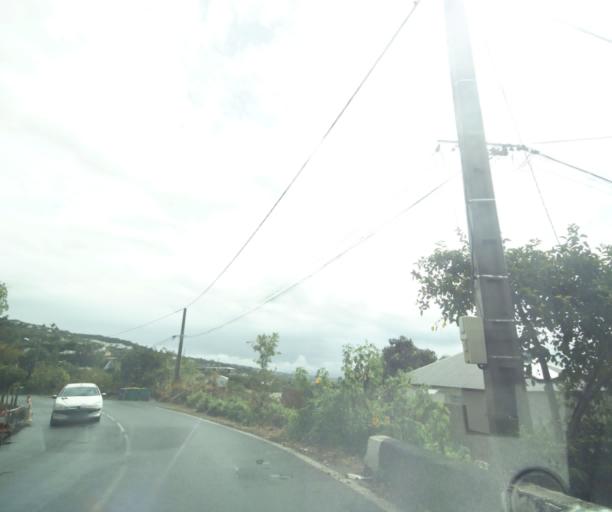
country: RE
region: Reunion
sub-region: Reunion
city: Saint-Paul
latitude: -20.9997
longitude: 55.3254
